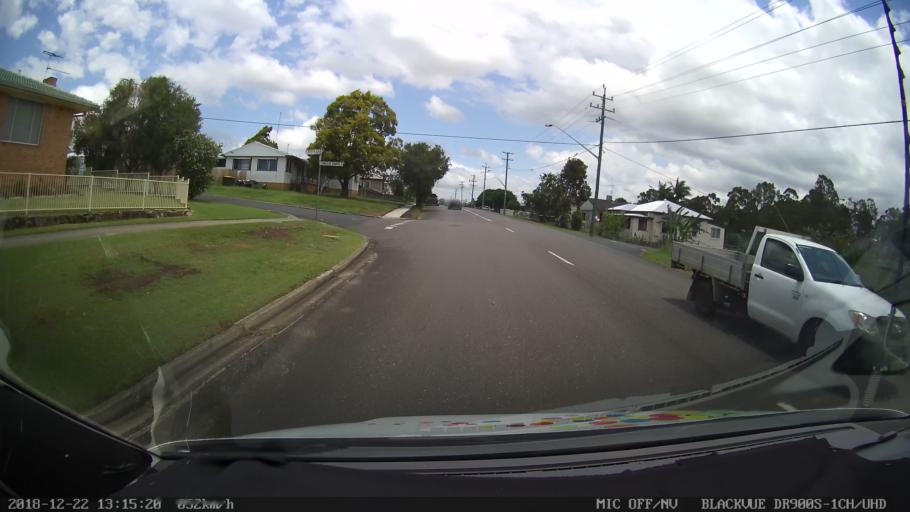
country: AU
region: New South Wales
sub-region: Clarence Valley
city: South Grafton
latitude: -29.7171
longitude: 152.9392
